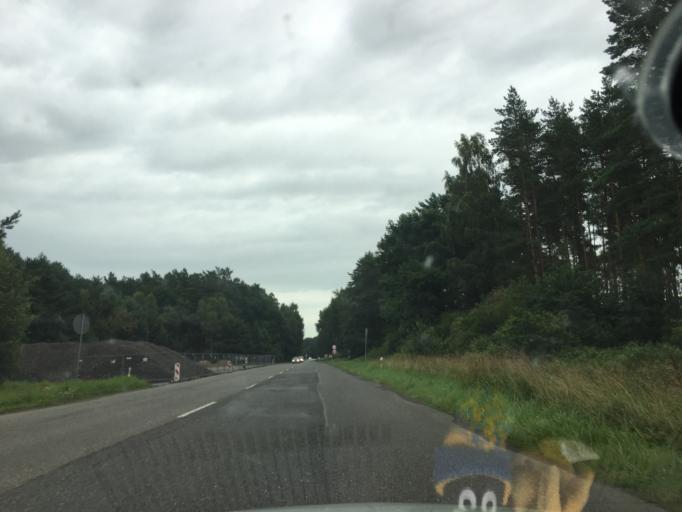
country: PL
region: West Pomeranian Voivodeship
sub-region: Powiat gryficki
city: Pobierowo
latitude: 54.0468
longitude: 14.9196
